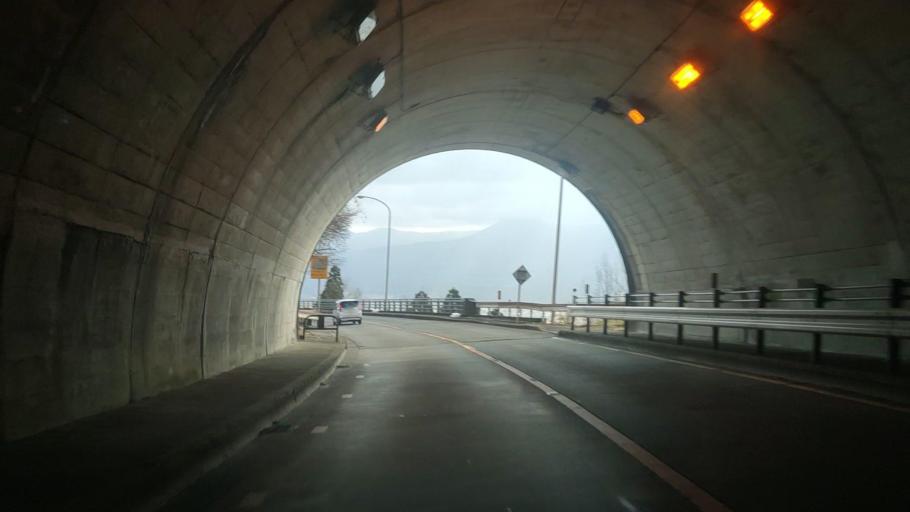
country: JP
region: Kumamoto
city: Hitoyoshi
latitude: 32.0719
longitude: 130.7967
